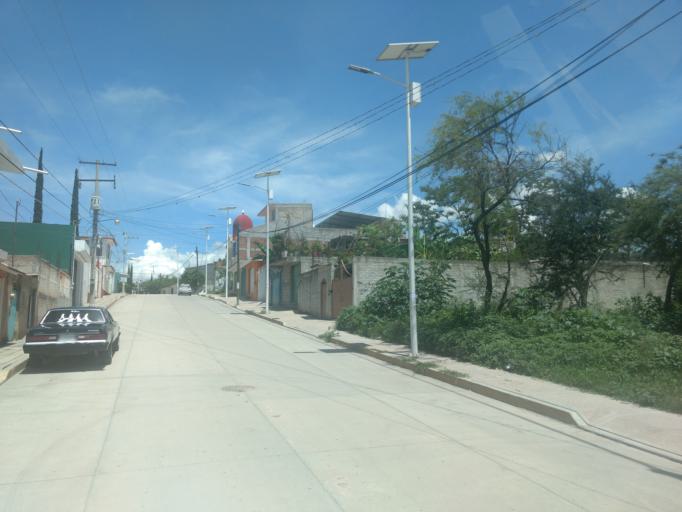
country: MX
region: Oaxaca
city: Ciudad de Huajuapam de Leon
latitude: 17.8150
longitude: -97.7901
